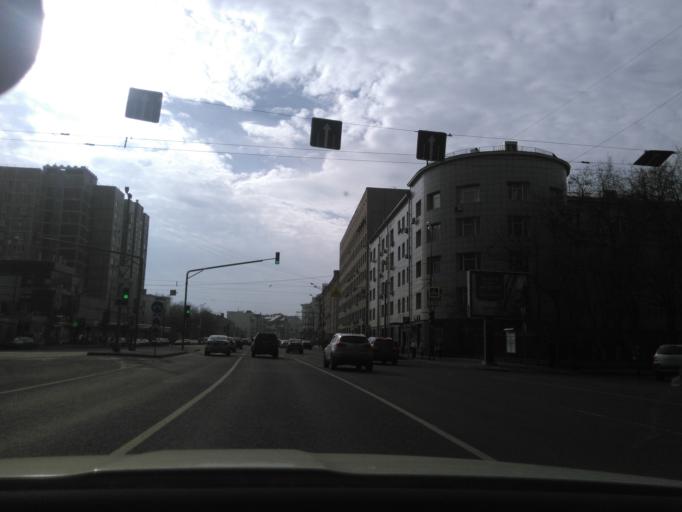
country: RU
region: Moscow
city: Mar'ina Roshcha
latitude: 55.7865
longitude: 37.5941
